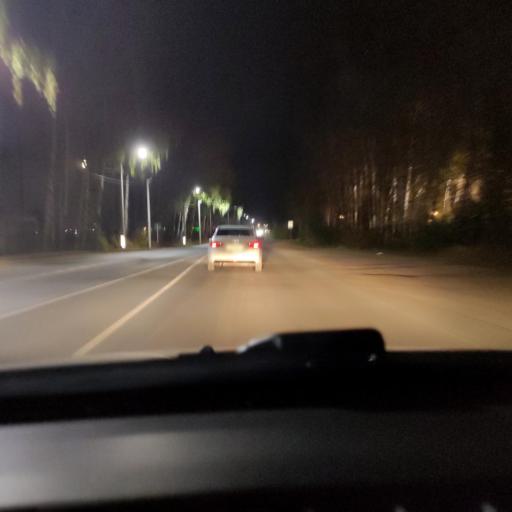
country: RU
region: Voronezj
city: Podgornoye
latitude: 51.7851
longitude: 39.1875
